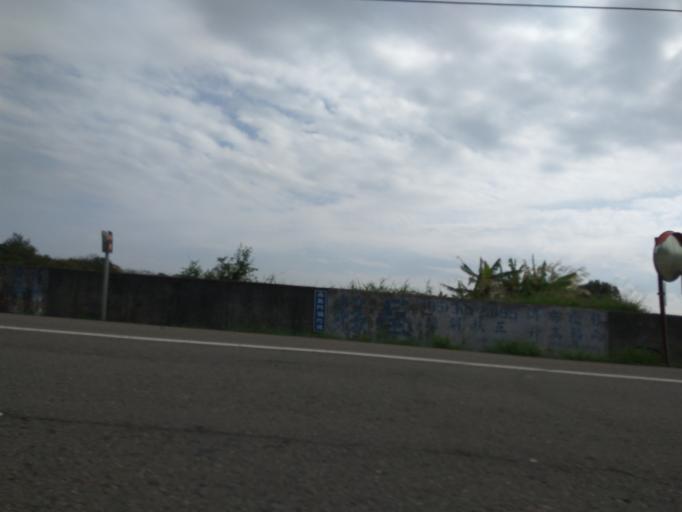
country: TW
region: Taiwan
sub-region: Hsinchu
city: Zhubei
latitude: 24.9585
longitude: 121.0134
